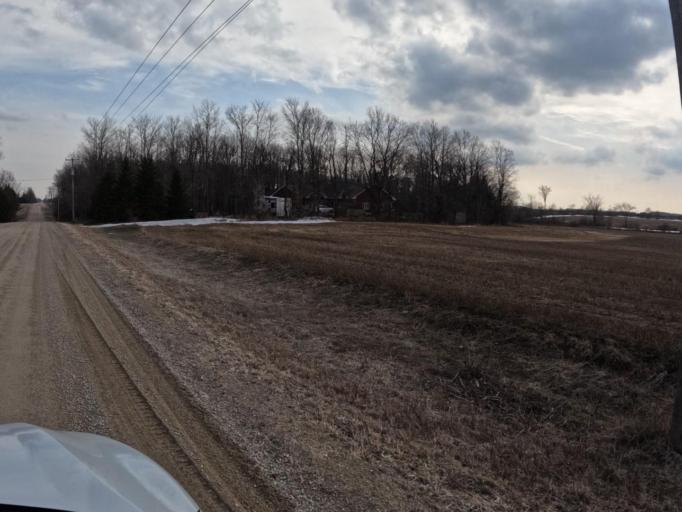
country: CA
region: Ontario
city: Shelburne
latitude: 43.9240
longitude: -80.3068
